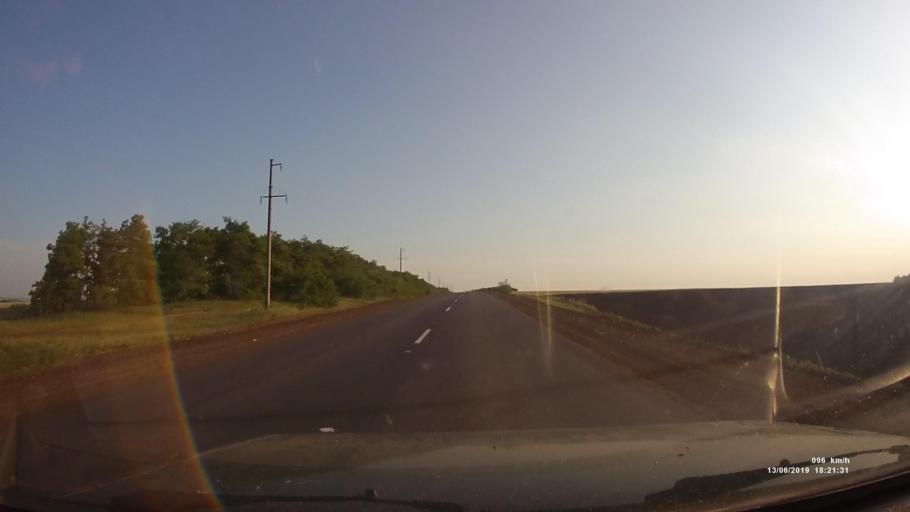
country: RU
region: Rostov
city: Kazanskaya
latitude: 49.8698
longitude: 41.2900
